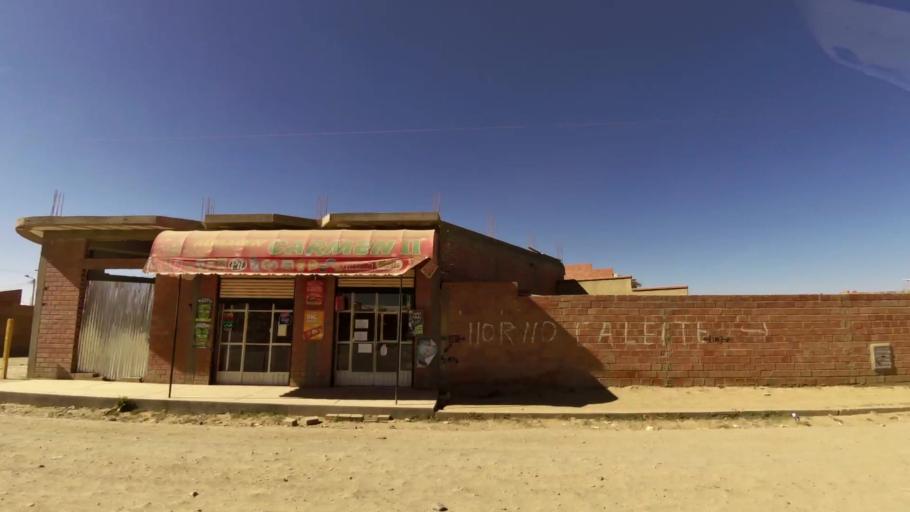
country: BO
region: La Paz
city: La Paz
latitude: -16.6236
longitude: -68.1899
